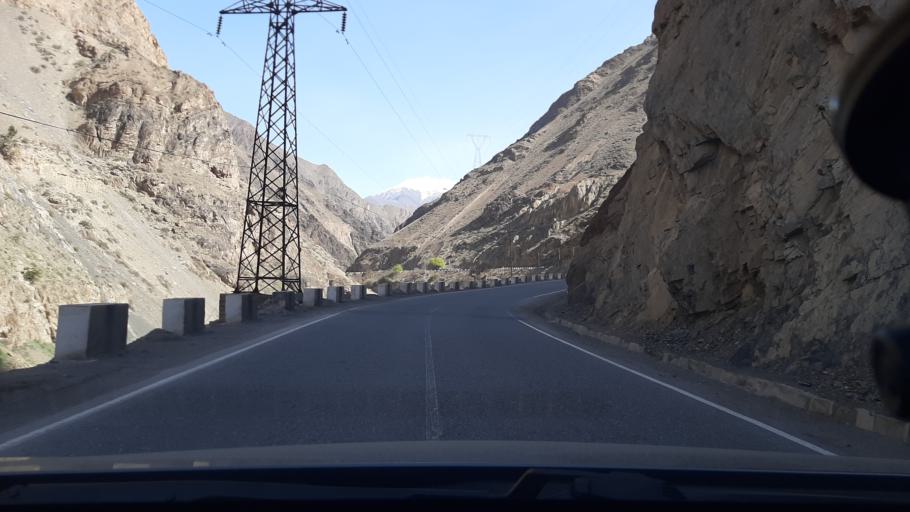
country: TJ
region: Viloyati Sughd
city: Ayni
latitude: 39.3411
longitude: 68.5537
